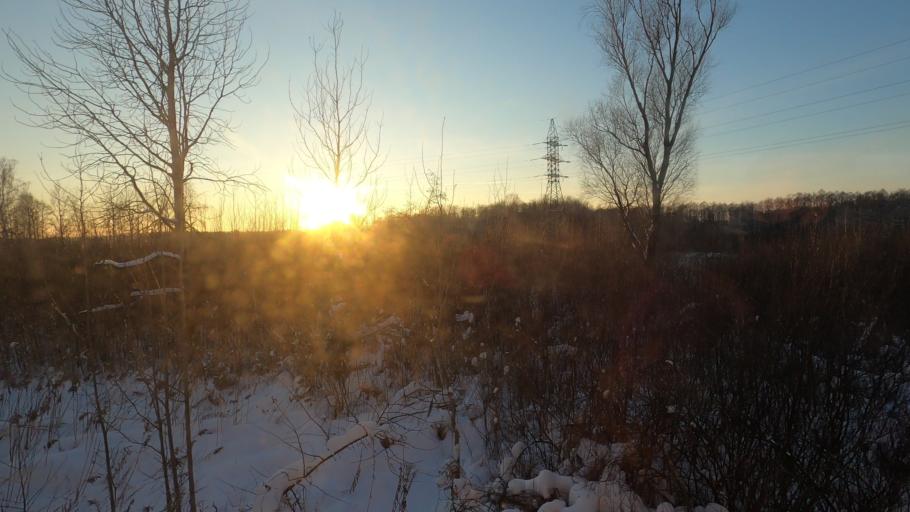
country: RU
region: Moskovskaya
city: Dmitrov
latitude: 56.3850
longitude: 37.5136
